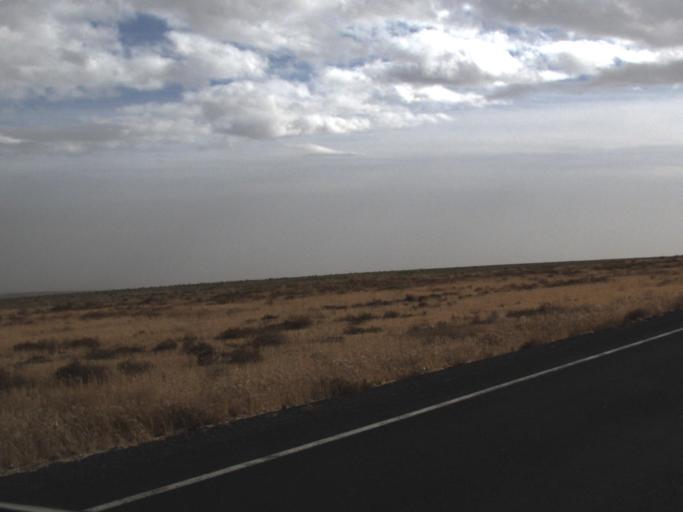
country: US
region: Washington
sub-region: Okanogan County
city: Coulee Dam
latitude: 47.4891
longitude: -118.7848
